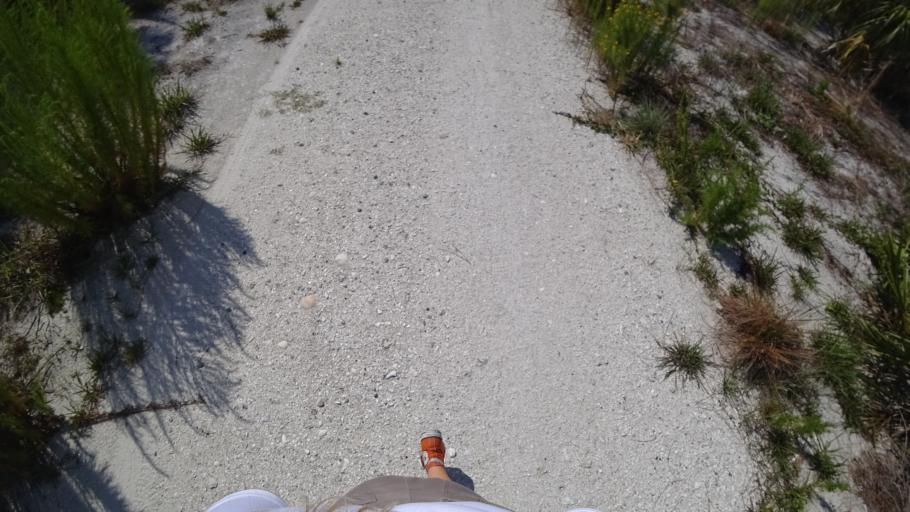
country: US
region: Florida
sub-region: Manatee County
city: Cortez
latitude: 27.5006
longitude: -82.6748
